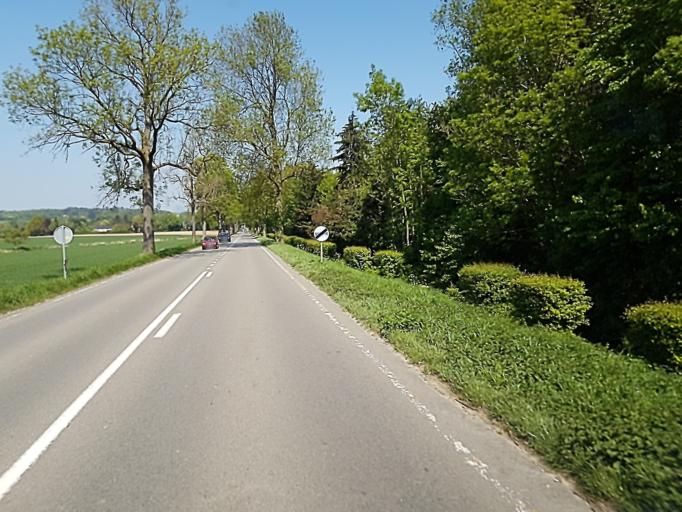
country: BE
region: Wallonia
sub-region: Province du Brabant Wallon
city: Grez-Doiceau
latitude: 50.7702
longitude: 4.7104
